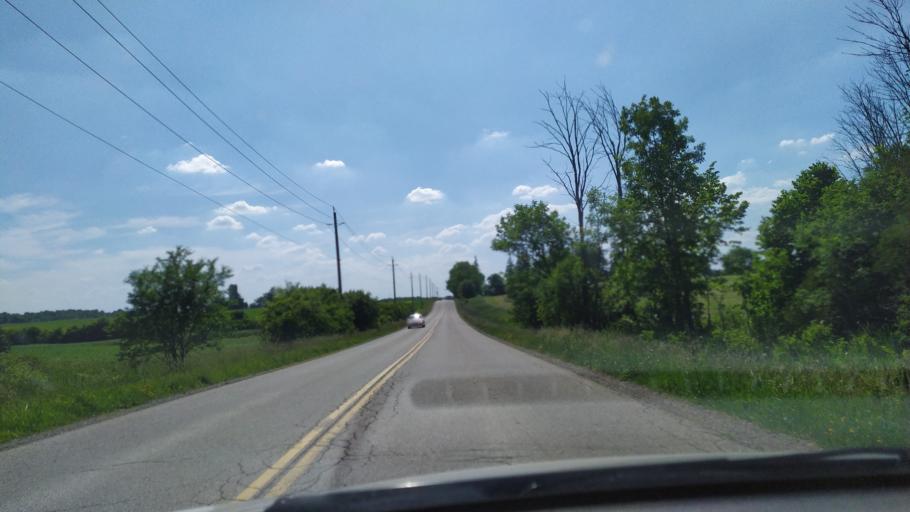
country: CA
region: Ontario
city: Kitchener
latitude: 43.3612
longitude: -80.6243
